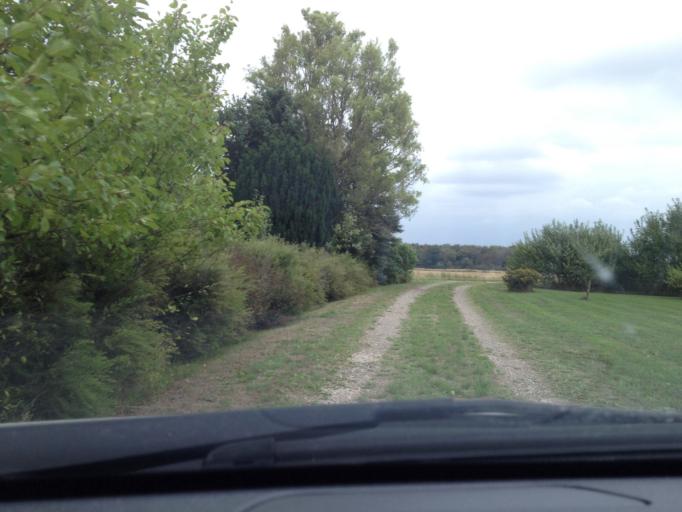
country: DK
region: South Denmark
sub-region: Haderslev Kommune
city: Starup
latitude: 55.2851
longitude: 9.5531
